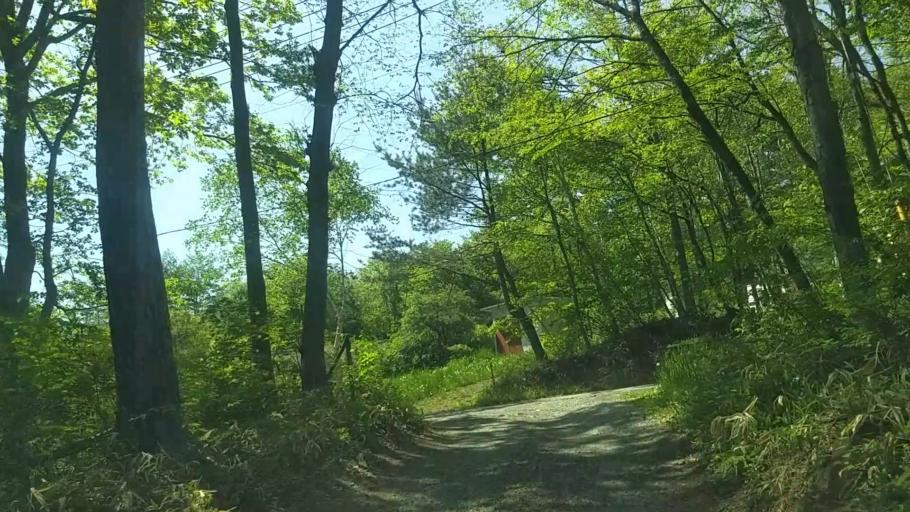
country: JP
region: Yamanashi
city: Nirasaki
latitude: 35.9125
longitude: 138.4308
